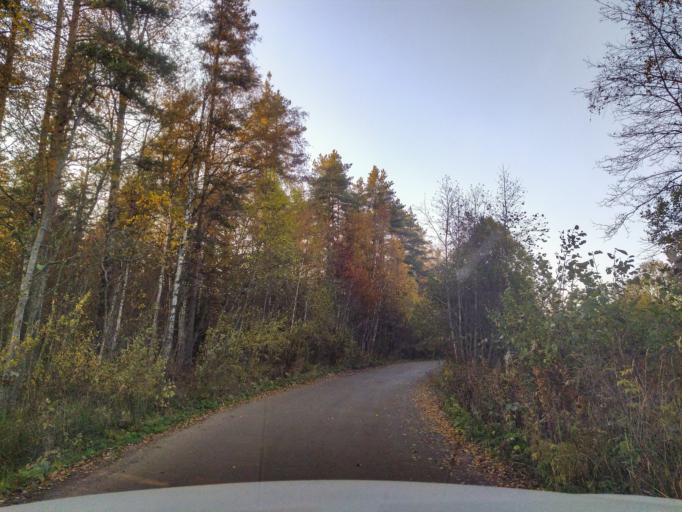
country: RU
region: Leningrad
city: Kuznechnoye
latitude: 61.3051
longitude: 30.0411
